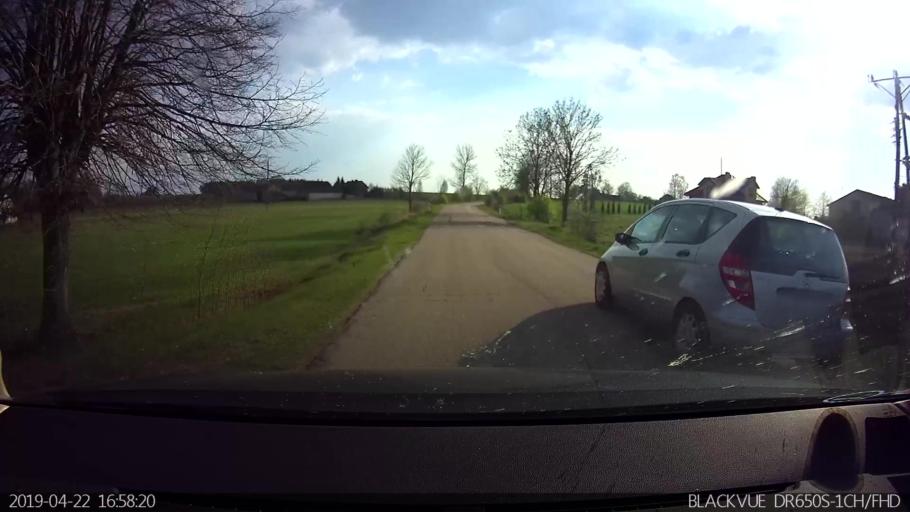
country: PL
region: Podlasie
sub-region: Powiat siemiatycki
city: Drohiczyn
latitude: 52.4723
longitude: 22.7526
